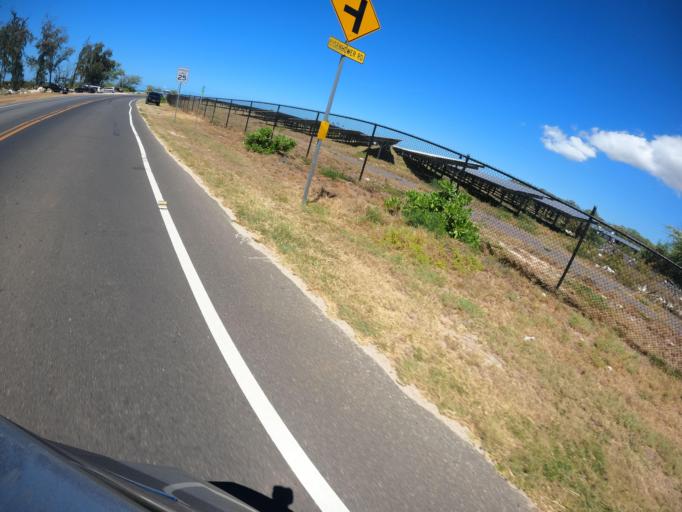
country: US
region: Hawaii
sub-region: Honolulu County
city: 'Ewa Villages
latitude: 21.3021
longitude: -158.0583
